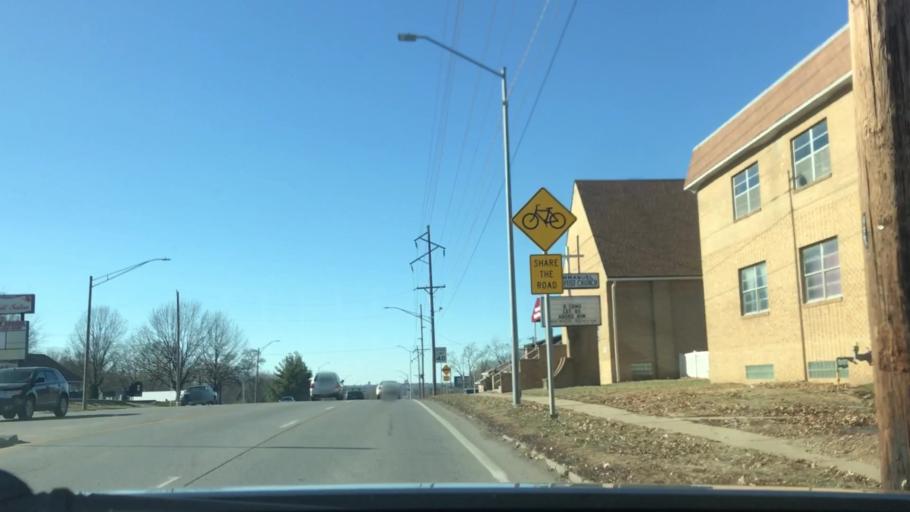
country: US
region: Missouri
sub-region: Jackson County
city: Independence
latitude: 39.0792
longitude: -94.4157
